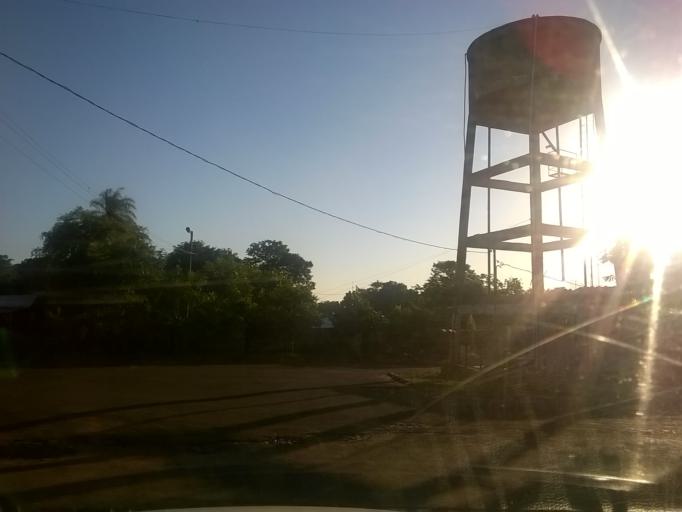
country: BR
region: Parana
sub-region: Foz Do Iguacu
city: Foz do Iguacu
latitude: -25.5676
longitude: -54.6138
